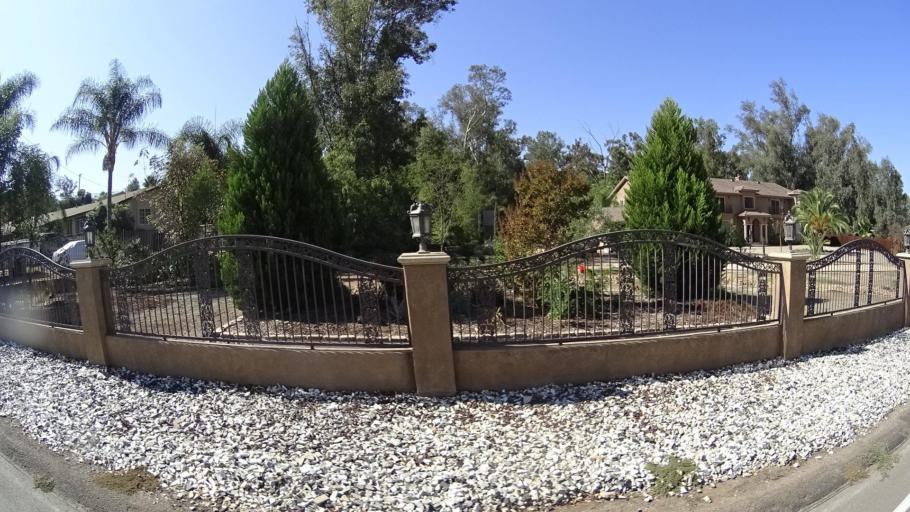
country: US
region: California
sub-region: San Diego County
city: Granite Hills
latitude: 32.7940
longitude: -116.9116
